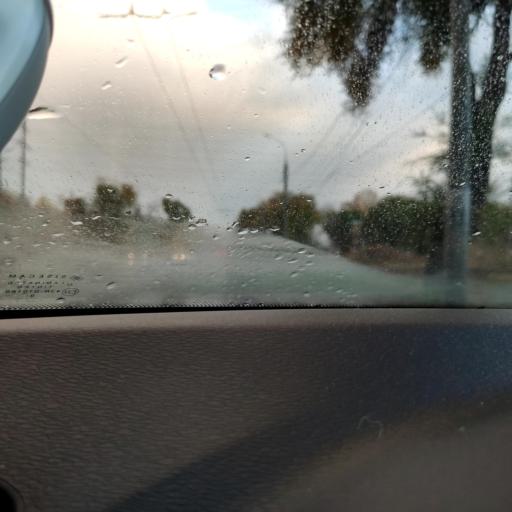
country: RU
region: Samara
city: Smyshlyayevka
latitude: 53.1980
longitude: 50.2878
